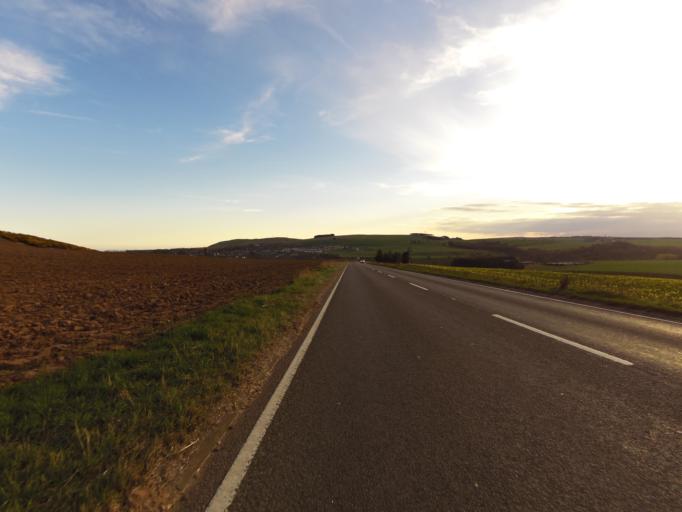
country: GB
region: Scotland
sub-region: Aberdeenshire
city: Inverbervie
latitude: 56.8529
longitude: -2.2743
